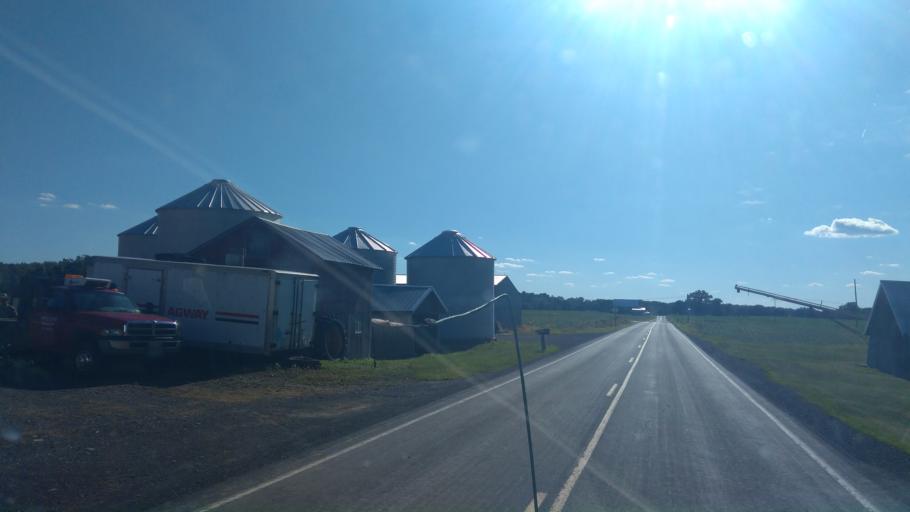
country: US
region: New York
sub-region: Wayne County
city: Clyde
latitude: 43.0011
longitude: -76.8845
